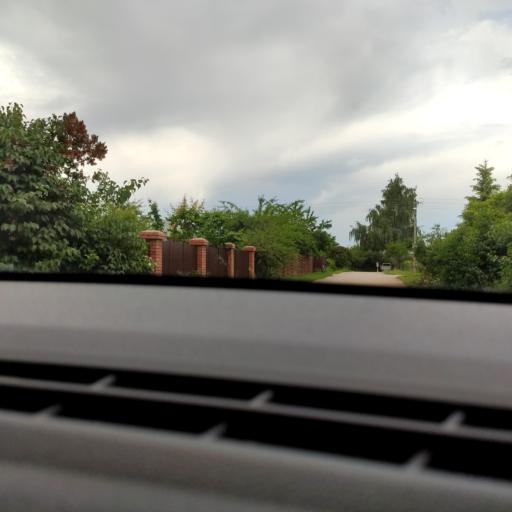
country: RU
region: Samara
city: Podstepki
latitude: 53.5124
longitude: 49.0760
